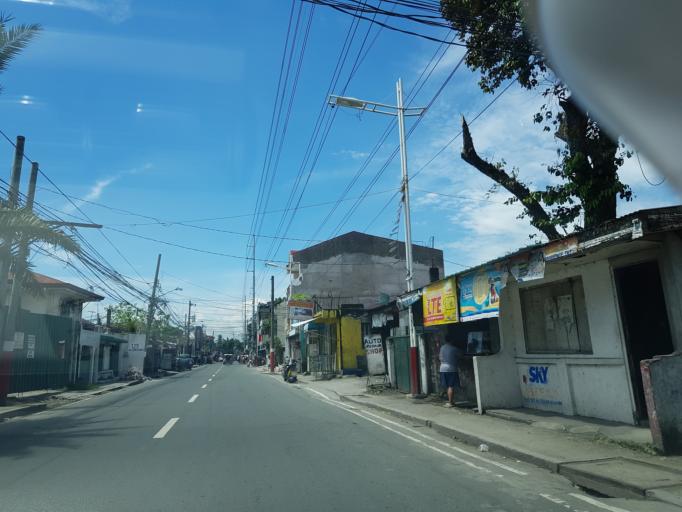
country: PH
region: Calabarzon
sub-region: Province of Rizal
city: Taguig
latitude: 14.5025
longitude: 121.0644
